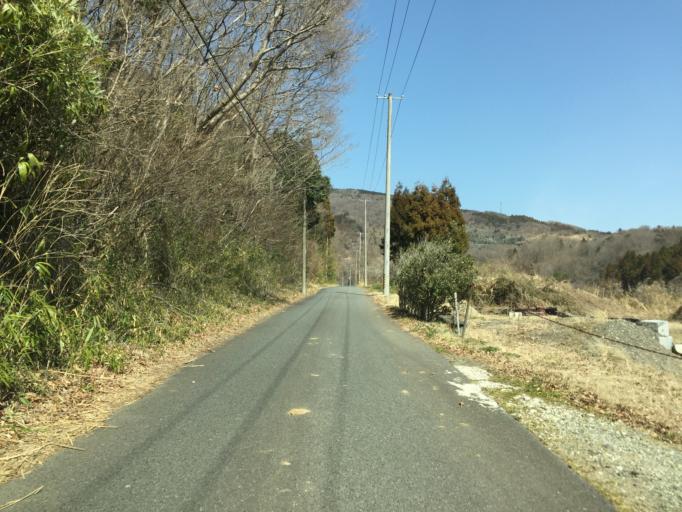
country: JP
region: Fukushima
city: Iwaki
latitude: 37.0023
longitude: 140.7936
